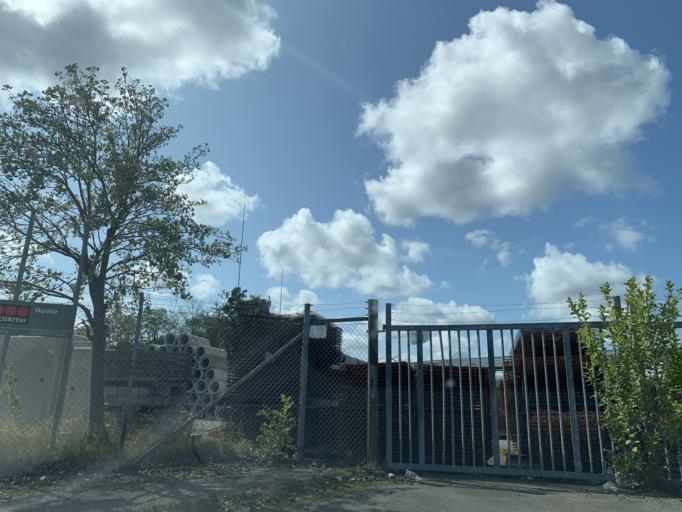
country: SE
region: Vaestra Goetaland
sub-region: Goteborg
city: Hammarkullen
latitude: 57.7679
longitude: 12.0252
